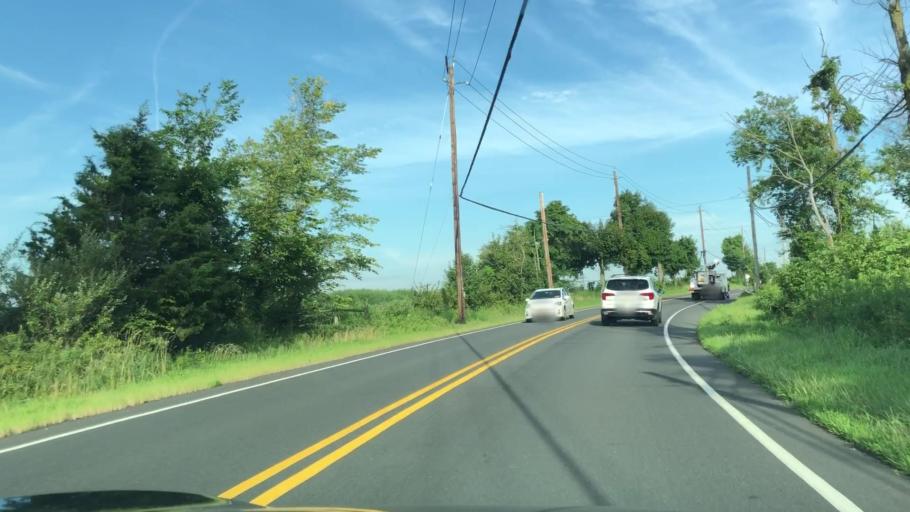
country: US
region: New Jersey
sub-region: Mercer County
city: Pennington
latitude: 40.3381
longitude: -74.7661
